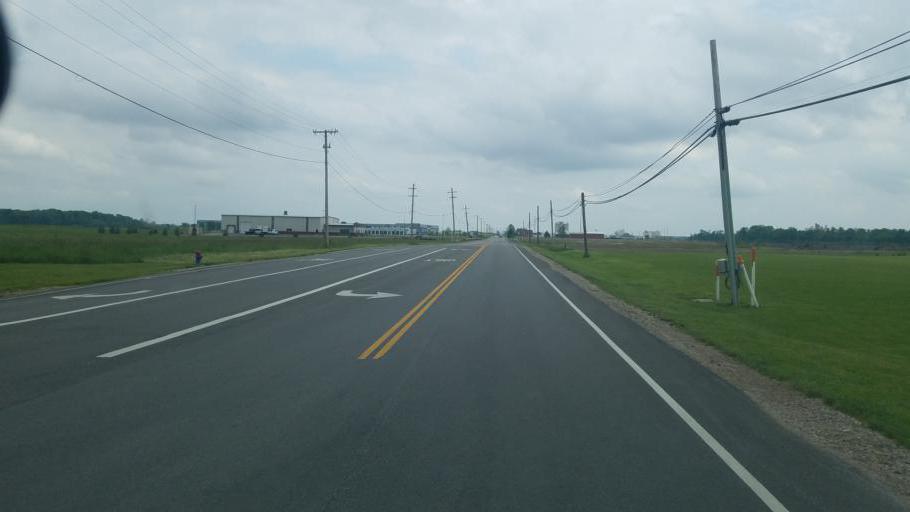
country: US
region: Ohio
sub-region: Union County
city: Marysville
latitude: 40.2245
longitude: -83.3399
